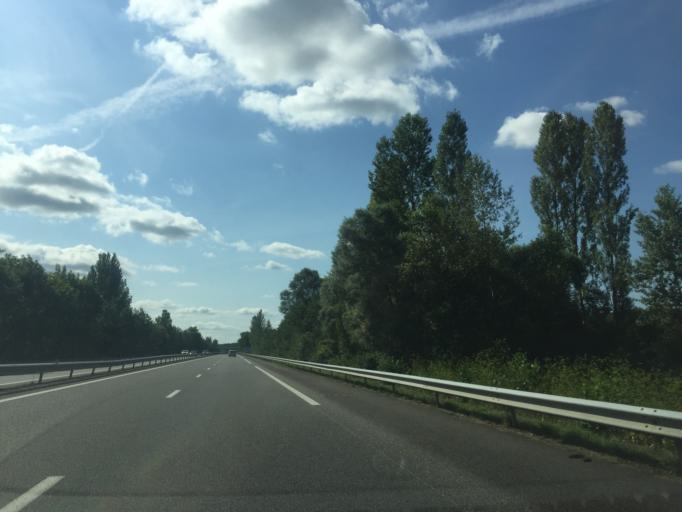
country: FR
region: Midi-Pyrenees
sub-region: Departement de la Haute-Garonne
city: Aurignac
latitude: 43.1262
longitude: 0.8662
